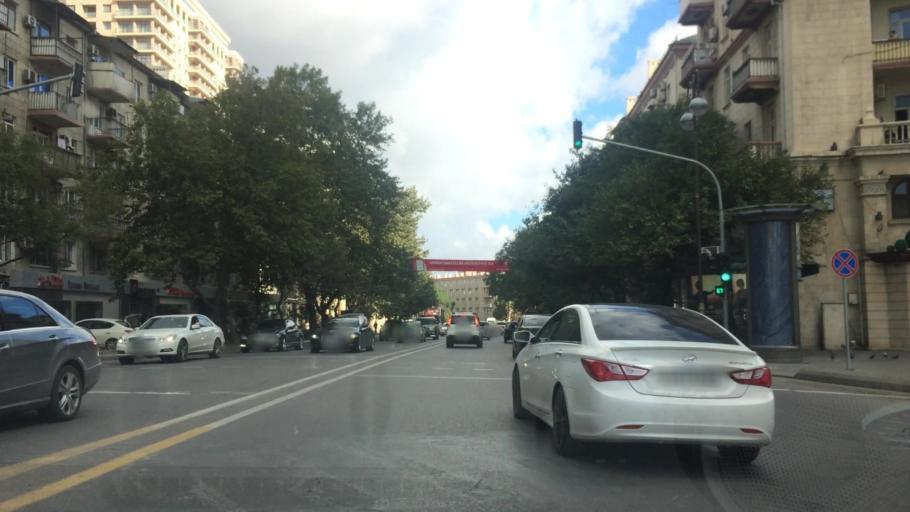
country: AZ
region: Baki
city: Badamdar
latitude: 40.3839
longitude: 49.8234
